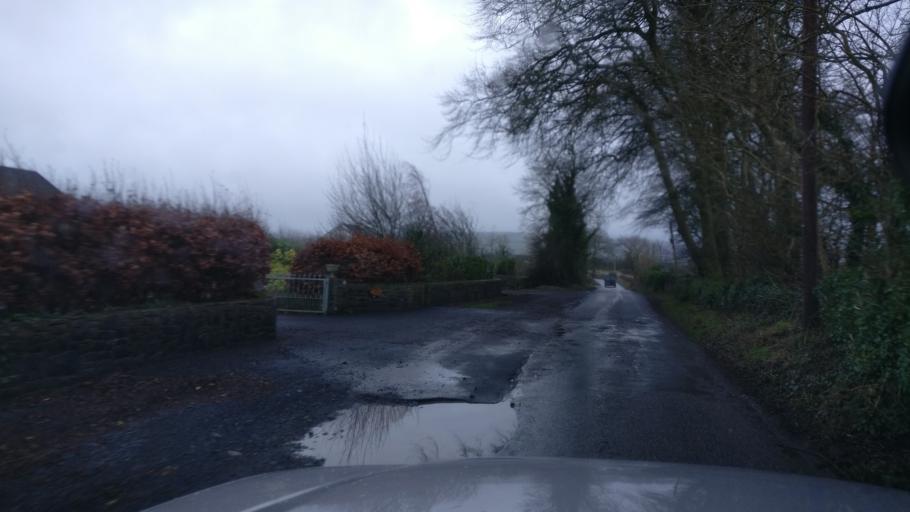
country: IE
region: Connaught
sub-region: County Galway
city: Loughrea
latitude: 53.1955
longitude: -8.6632
